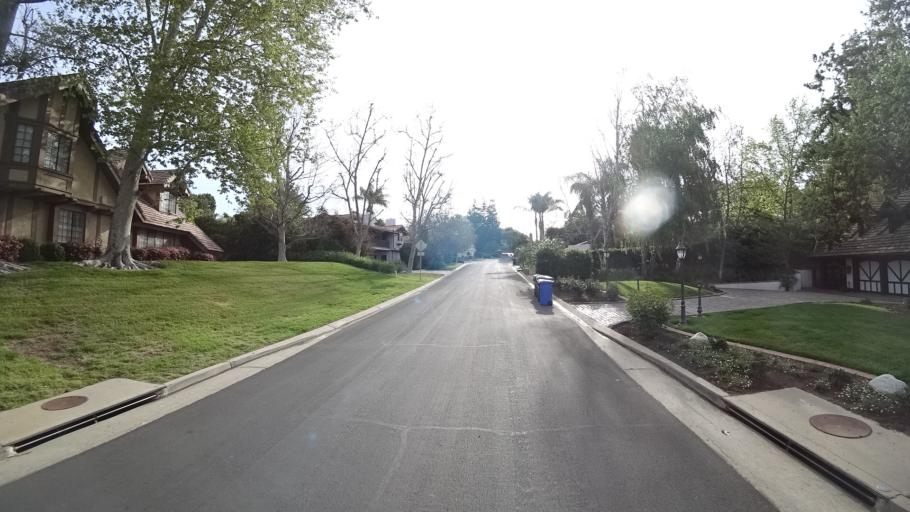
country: US
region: California
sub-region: Ventura County
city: Thousand Oaks
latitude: 34.1936
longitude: -118.8166
